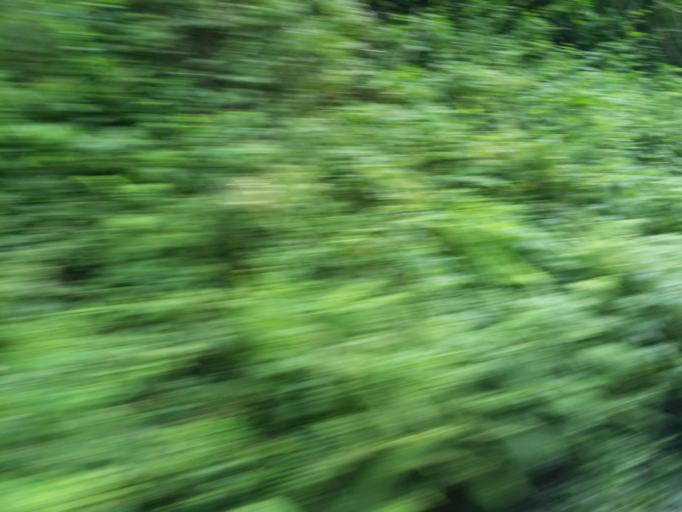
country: GB
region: England
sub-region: Cornwall
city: Par
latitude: 50.3697
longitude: -4.6831
